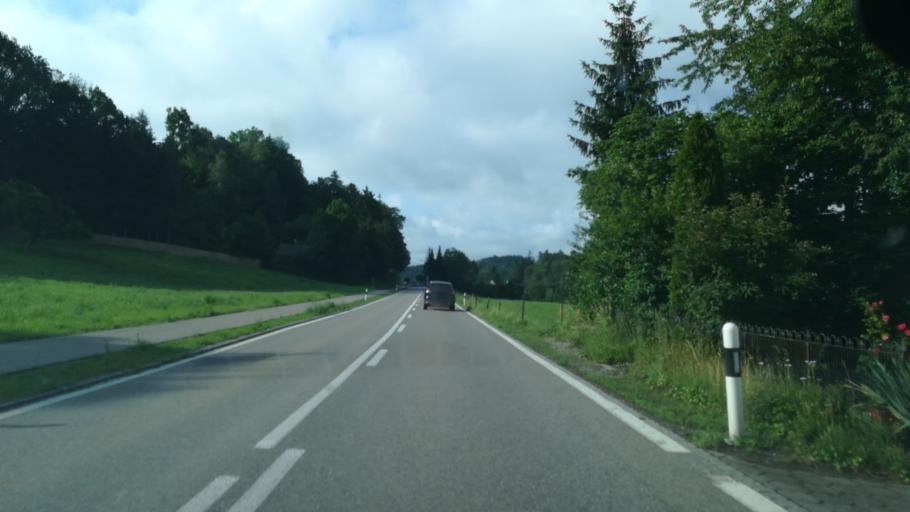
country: CH
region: Thurgau
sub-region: Weinfelden District
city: Sulgen
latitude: 47.5102
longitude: 9.2104
